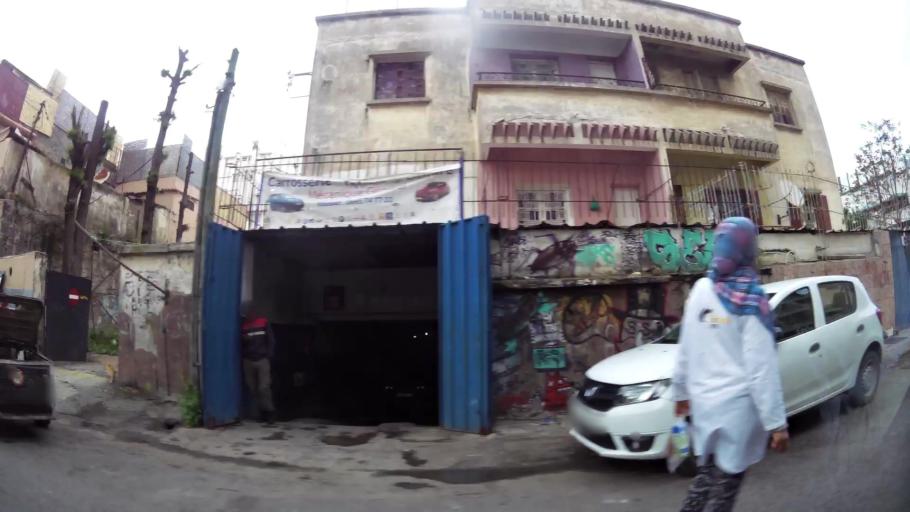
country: MA
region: Grand Casablanca
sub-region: Casablanca
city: Casablanca
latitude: 33.5704
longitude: -7.6237
